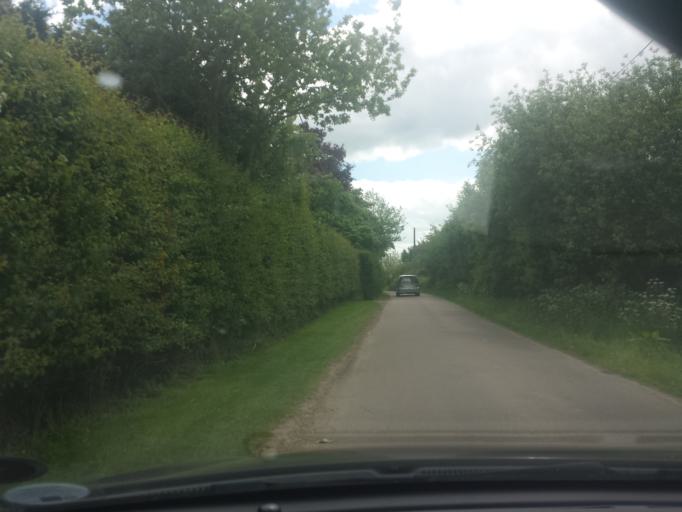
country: GB
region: England
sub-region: Essex
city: Little Clacton
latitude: 51.8617
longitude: 1.1398
